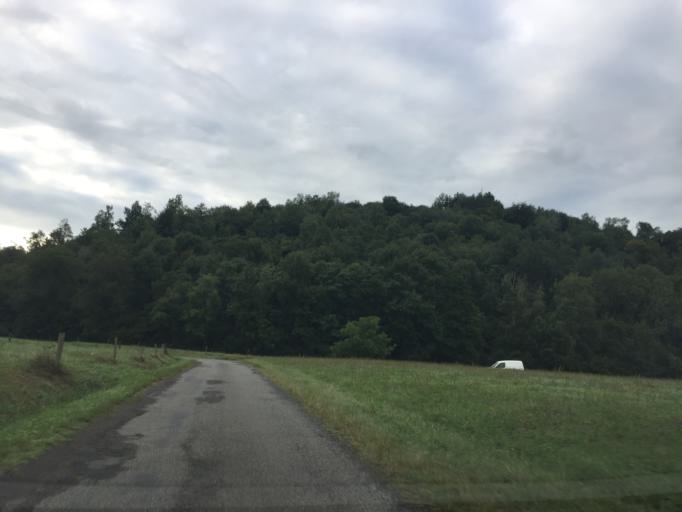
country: FR
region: Midi-Pyrenees
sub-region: Departement des Hautes-Pyrenees
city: Tournay
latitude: 43.1737
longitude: 0.2364
